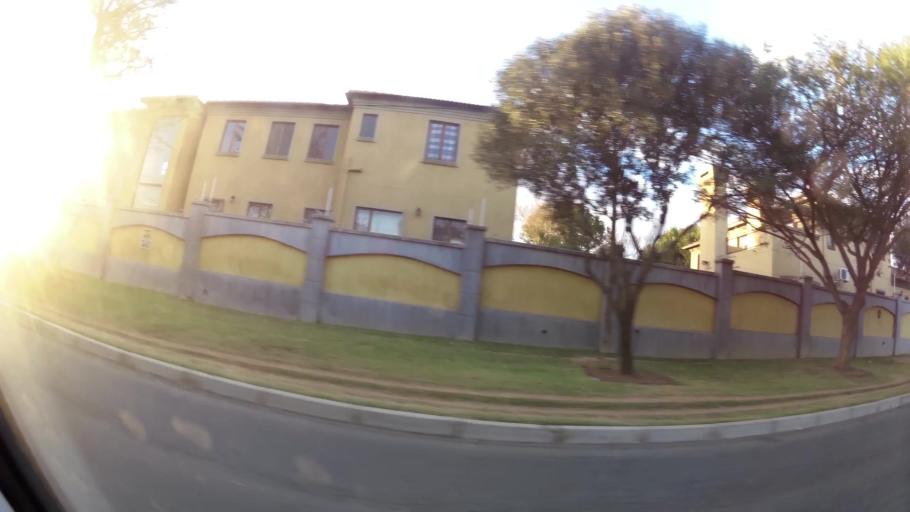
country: ZA
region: Gauteng
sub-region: City of Johannesburg Metropolitan Municipality
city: Diepsloot
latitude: -26.0167
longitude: 27.9813
